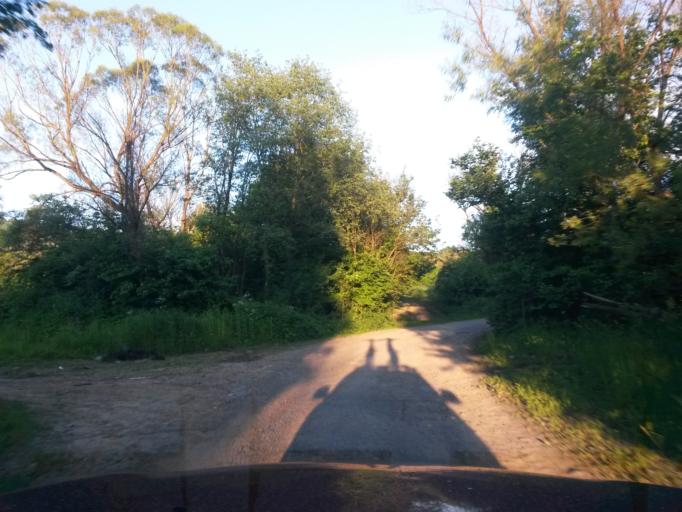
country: UA
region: Zakarpattia
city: Velykyi Bereznyi
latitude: 48.8555
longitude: 22.3619
